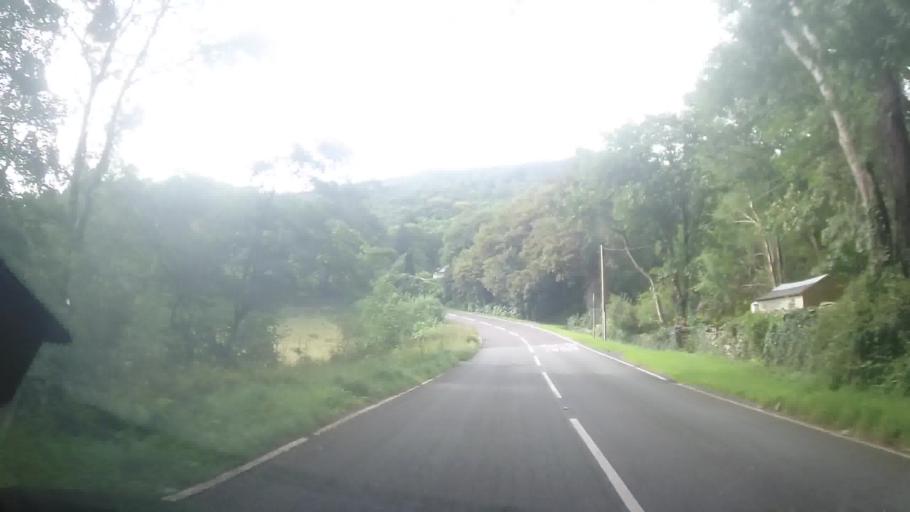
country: GB
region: Wales
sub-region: Gwynedd
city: Barmouth
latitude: 52.7425
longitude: -3.9996
